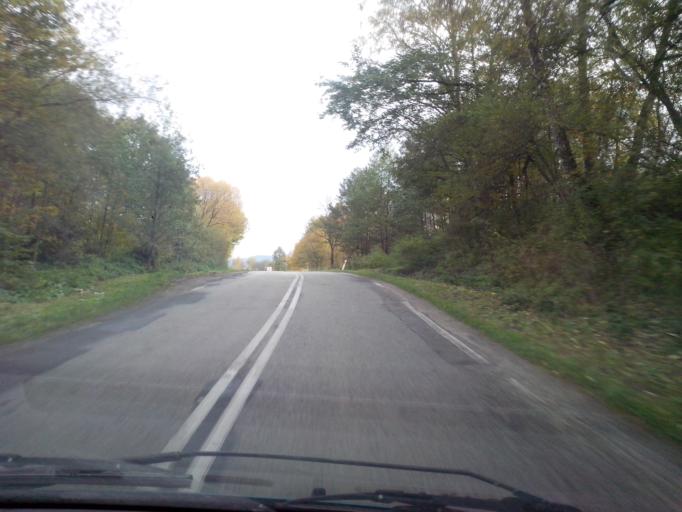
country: PL
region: Subcarpathian Voivodeship
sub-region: Powiat strzyzowski
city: Wisniowa
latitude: 49.8758
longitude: 21.6497
